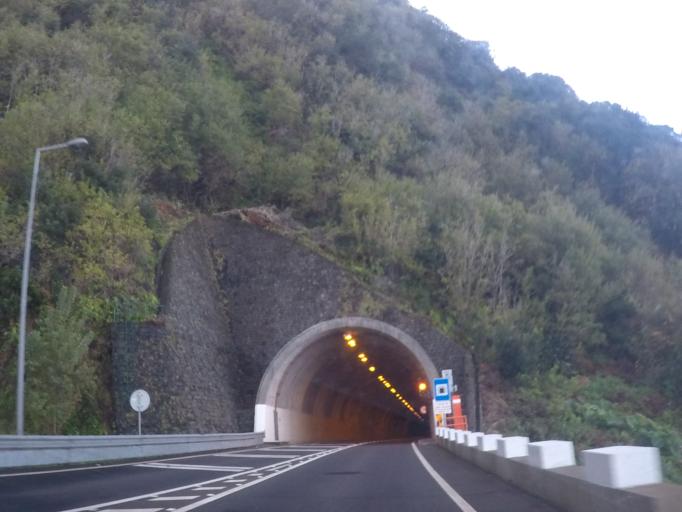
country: PT
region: Madeira
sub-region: Sao Vicente
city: Sao Vicente
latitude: 32.8137
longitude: -17.0234
